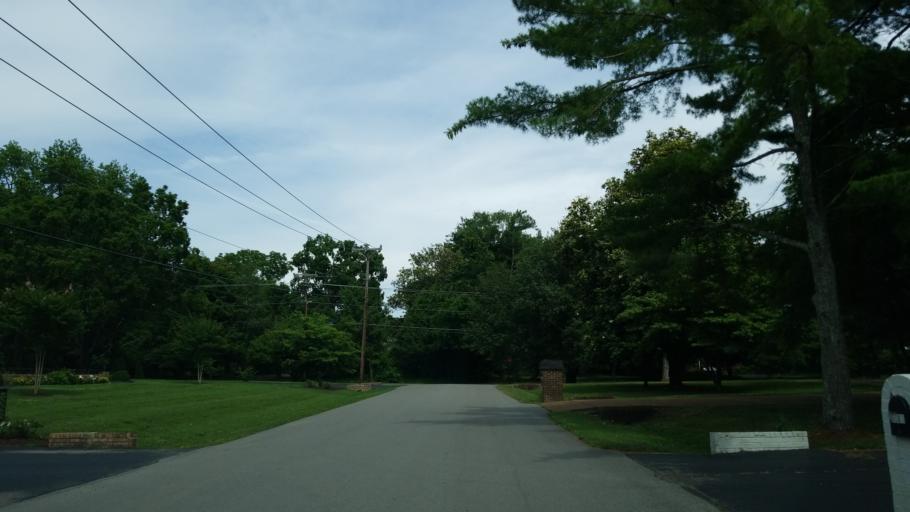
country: US
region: Tennessee
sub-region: Davidson County
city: Forest Hills
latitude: 36.0349
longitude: -86.8229
